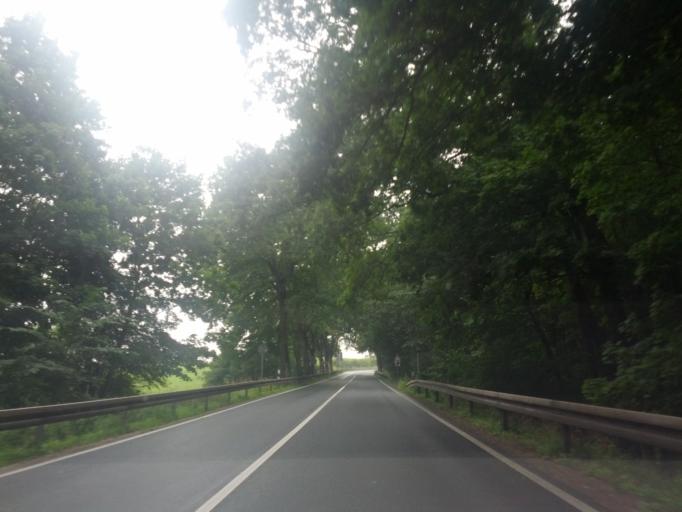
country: DE
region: Mecklenburg-Vorpommern
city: Sellin
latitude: 53.9244
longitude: 11.5977
